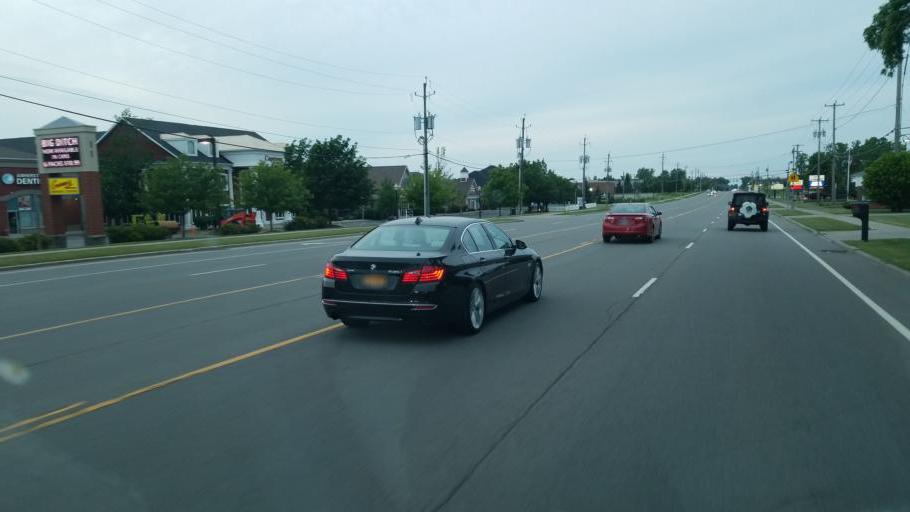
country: US
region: New York
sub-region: Erie County
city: Harris Hill
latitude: 43.0010
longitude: -78.6968
